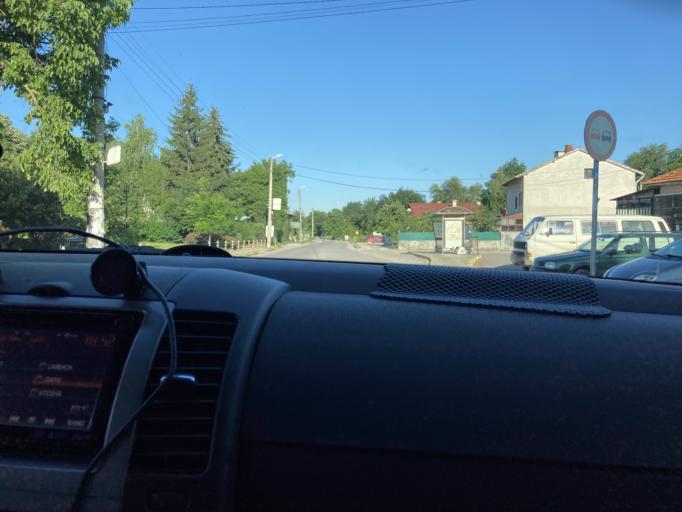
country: BG
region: Sofiya
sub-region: Obshtina Slivnitsa
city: Slivnitsa
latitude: 42.8473
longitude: 22.9897
